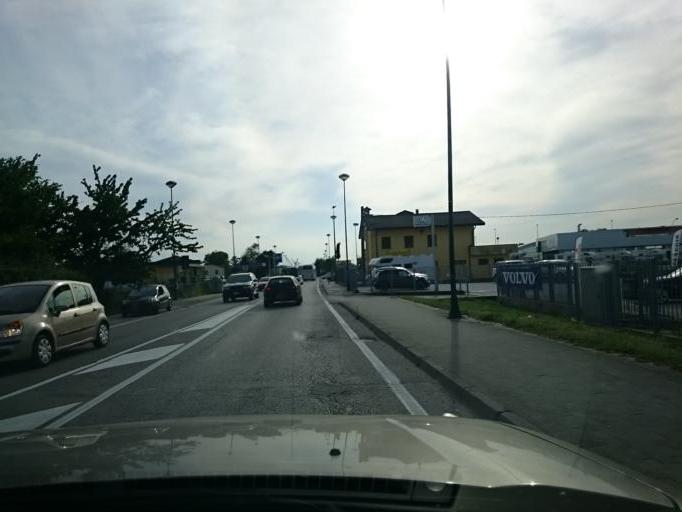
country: IT
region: Veneto
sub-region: Provincia di Venezia
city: Campalto
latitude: 45.4845
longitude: 12.2826
